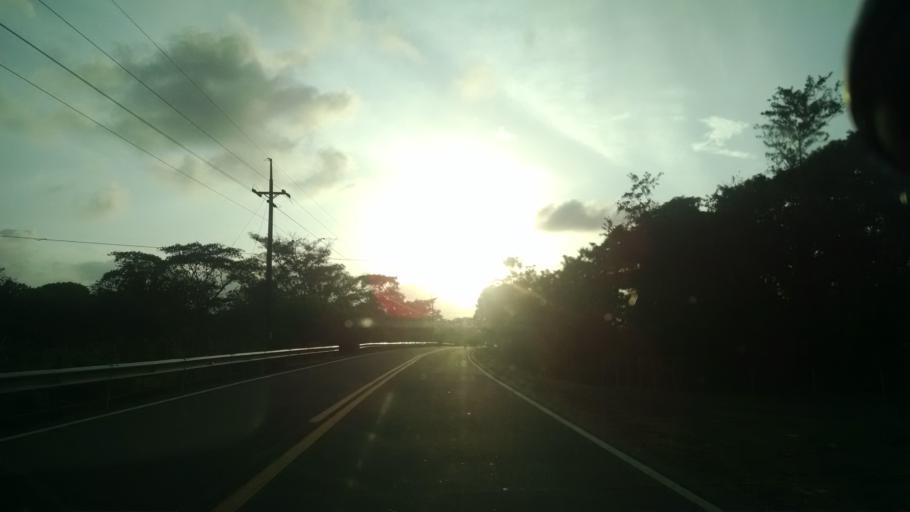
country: CO
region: Antioquia
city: San Juan de Uraba
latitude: 8.7374
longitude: -76.5599
